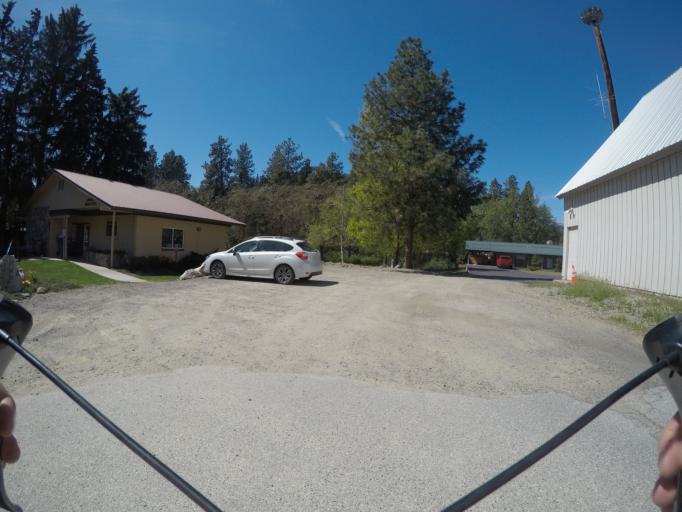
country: US
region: Washington
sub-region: Chelan County
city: Leavenworth
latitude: 47.5697
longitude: -120.6040
